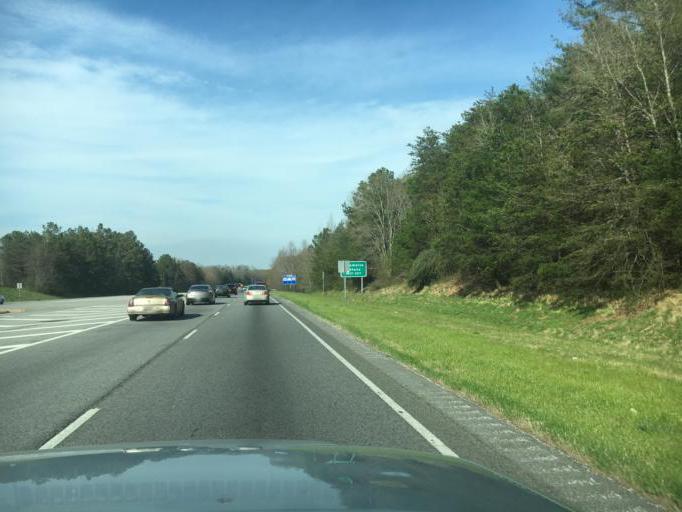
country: US
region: Georgia
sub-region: Habersham County
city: Baldwin
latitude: 34.5025
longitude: -83.5705
